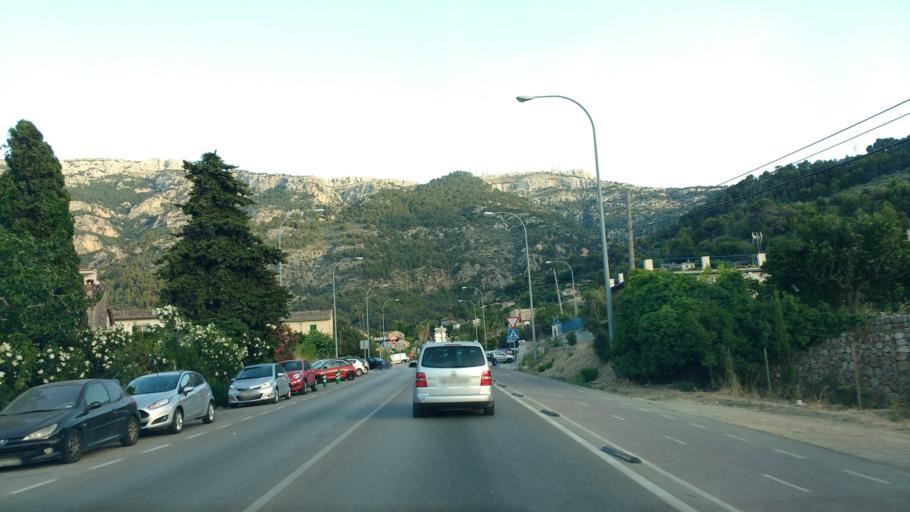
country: ES
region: Balearic Islands
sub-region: Illes Balears
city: Soller
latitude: 39.7676
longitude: 2.7076
